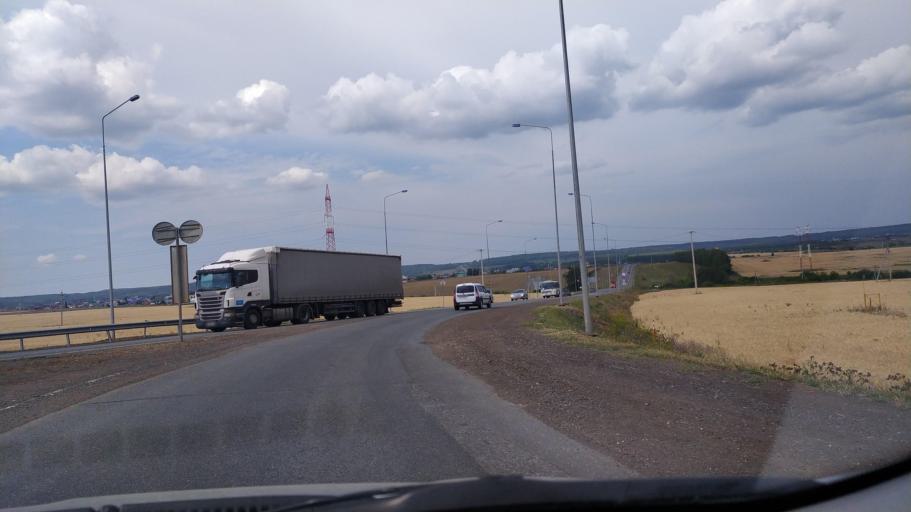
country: RU
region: Tatarstan
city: Al'met'yevsk
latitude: 54.9018
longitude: 52.2257
